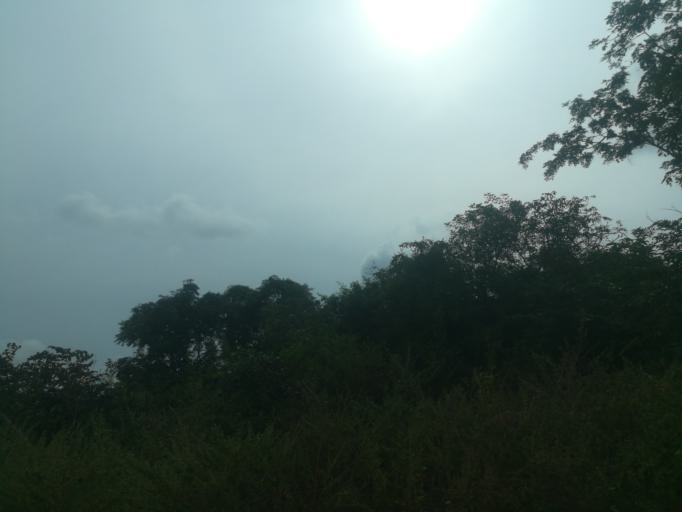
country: NG
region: Ogun
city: Ayetoro
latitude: 7.2704
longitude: 3.1035
